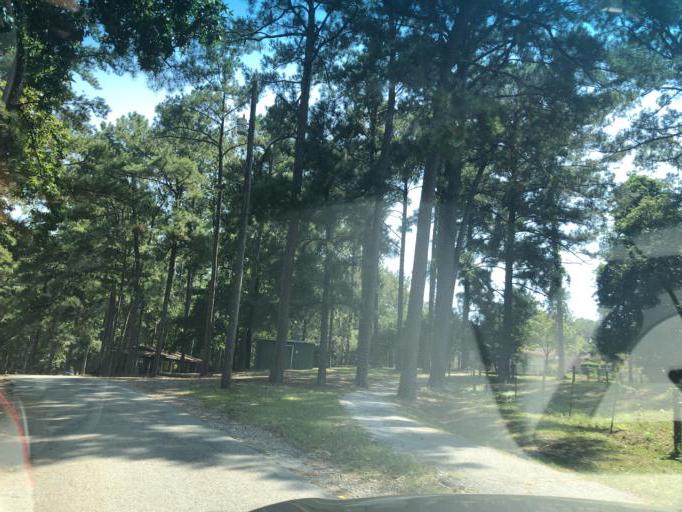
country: US
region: Georgia
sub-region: Muscogee County
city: Columbus
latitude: 32.5097
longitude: -84.9147
